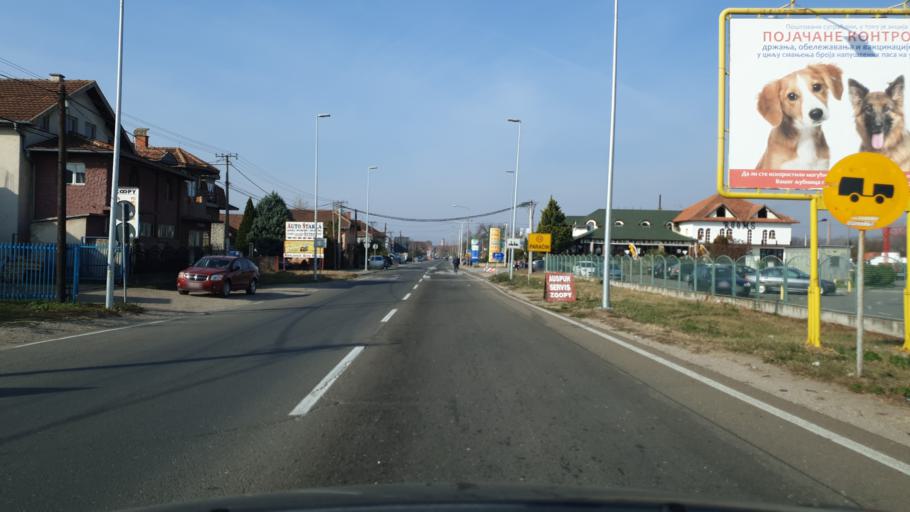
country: RS
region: Central Serbia
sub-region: Pomoravski Okrug
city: Paracin
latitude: 43.8578
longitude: 21.4323
